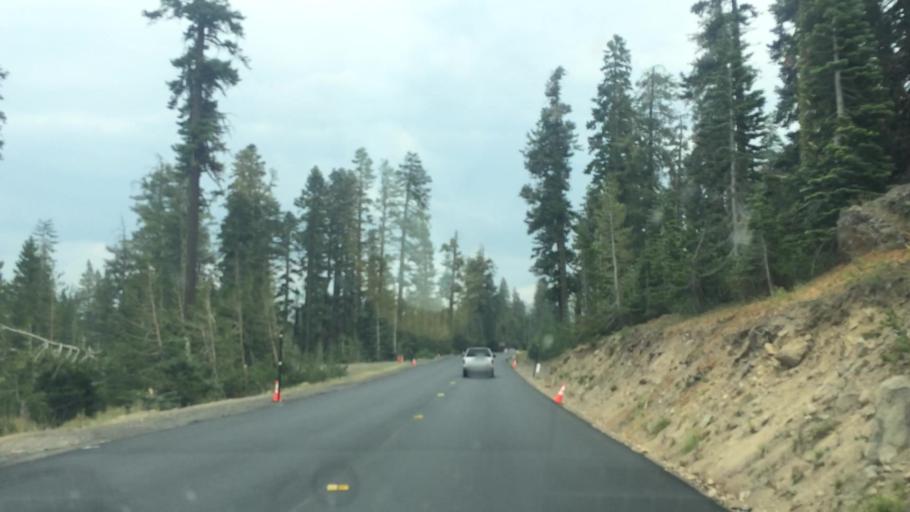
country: US
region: California
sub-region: El Dorado County
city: South Lake Tahoe
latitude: 38.7032
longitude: -120.0895
